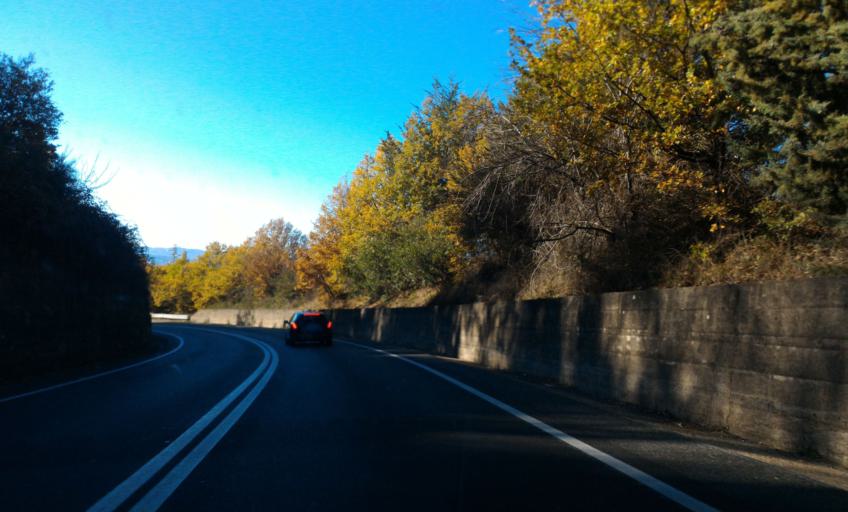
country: IT
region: Calabria
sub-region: Provincia di Cosenza
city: Rovito
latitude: 39.3065
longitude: 16.3104
